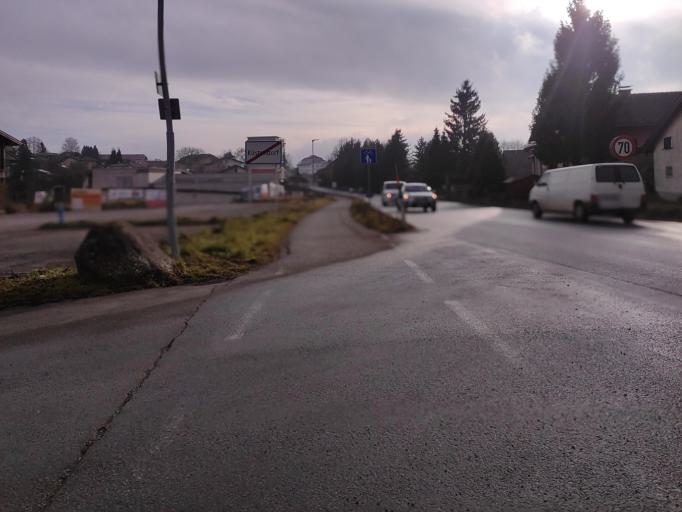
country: AT
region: Salzburg
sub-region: Politischer Bezirk Salzburg-Umgebung
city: Kostendorf
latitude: 47.9553
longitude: 13.2043
